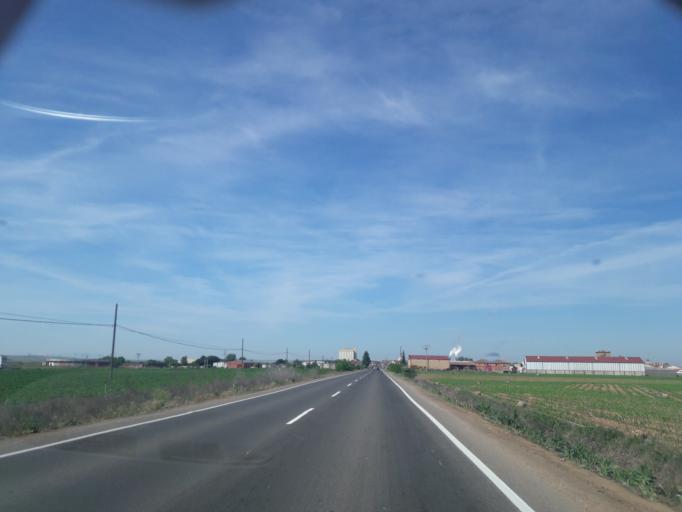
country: ES
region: Castille and Leon
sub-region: Provincia de Salamanca
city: Babilafuente
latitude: 40.9792
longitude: -5.4186
